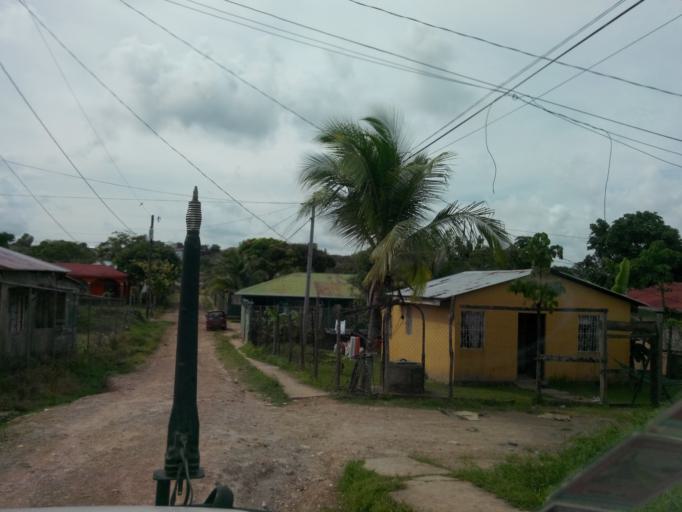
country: NI
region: Atlantico Sur
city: Bluefields
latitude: 12.0015
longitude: -83.7681
